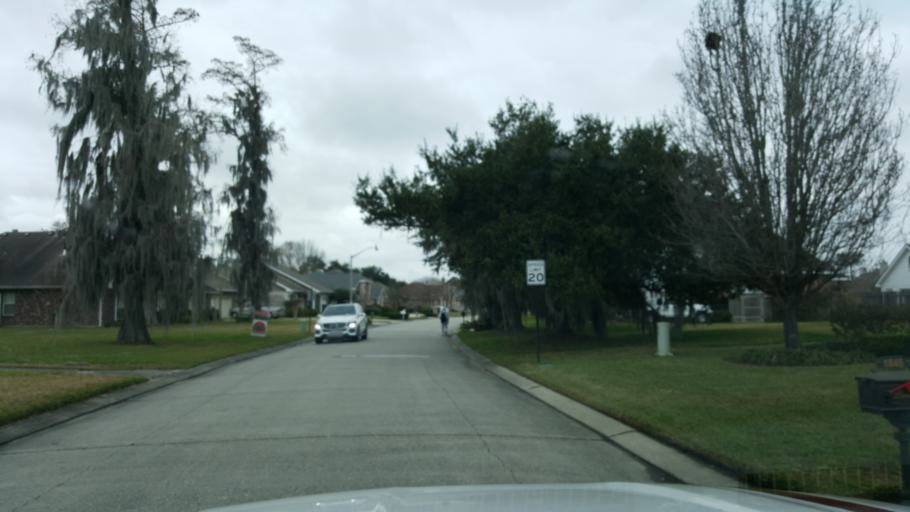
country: US
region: Louisiana
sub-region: Jefferson Parish
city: Woodmere
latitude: 29.8738
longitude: -90.0803
